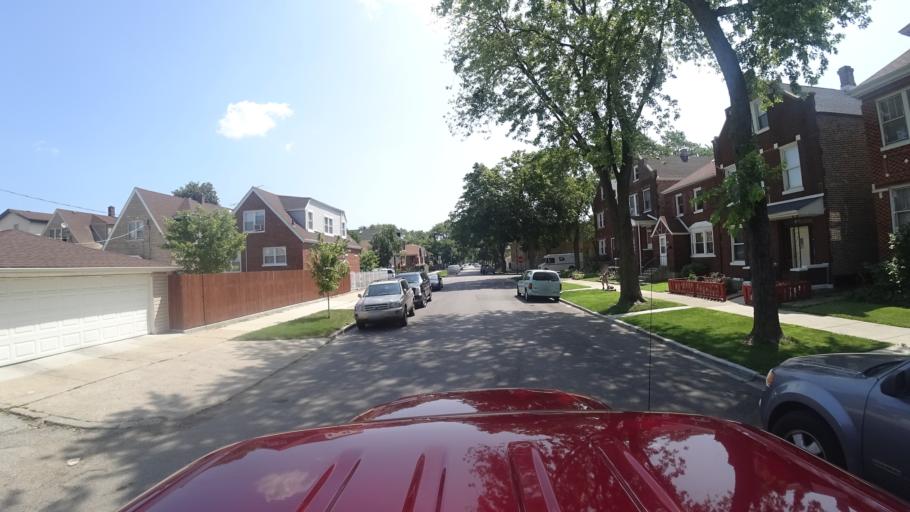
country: US
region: Illinois
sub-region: Cook County
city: Hometown
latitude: 41.7972
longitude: -87.6994
